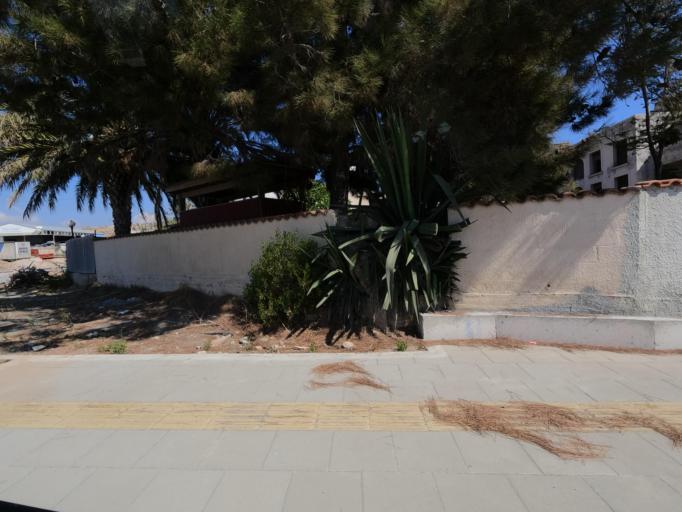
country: CY
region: Pafos
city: Paphos
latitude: 34.7713
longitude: 32.4489
